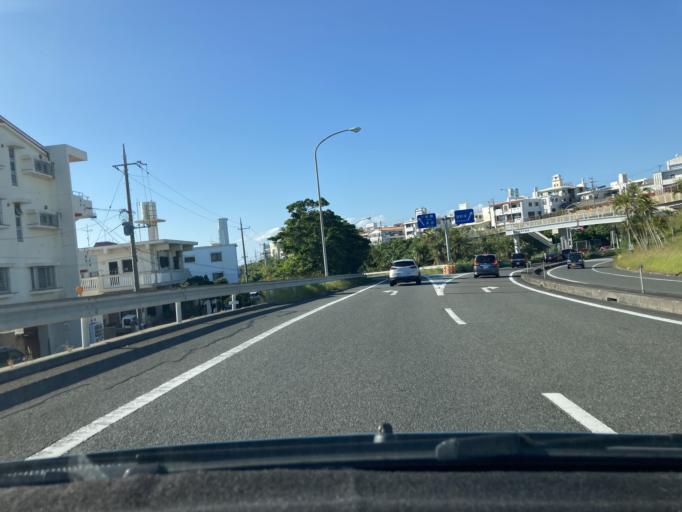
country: JP
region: Okinawa
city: Ginowan
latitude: 26.2485
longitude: 127.7470
